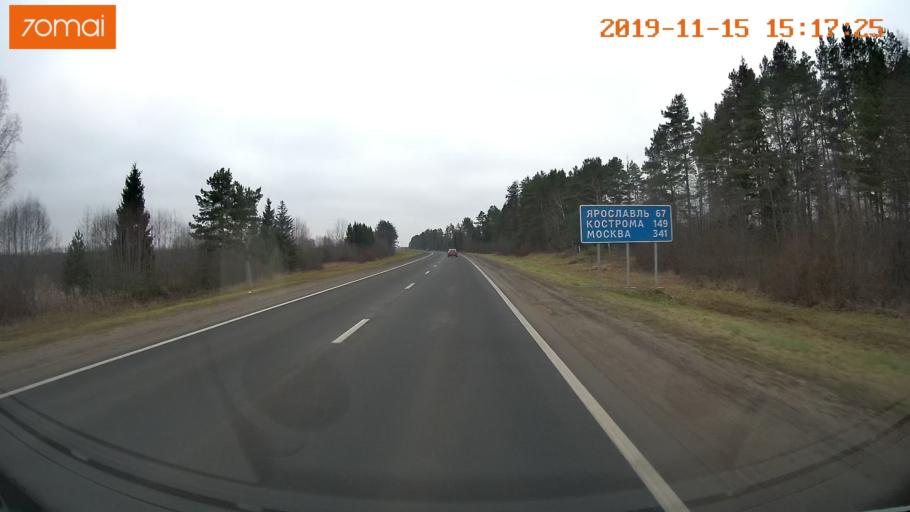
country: RU
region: Jaroslavl
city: Danilov
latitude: 58.2611
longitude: 40.1817
